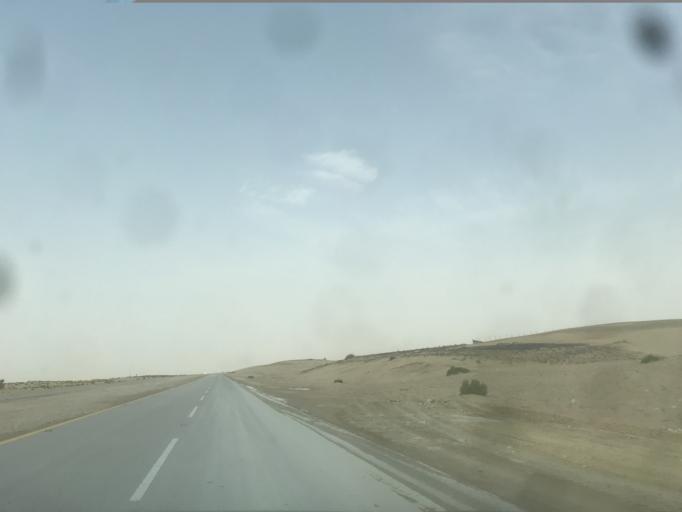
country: SA
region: Eastern Province
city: Abqaiq
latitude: 25.9098
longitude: 49.8844
